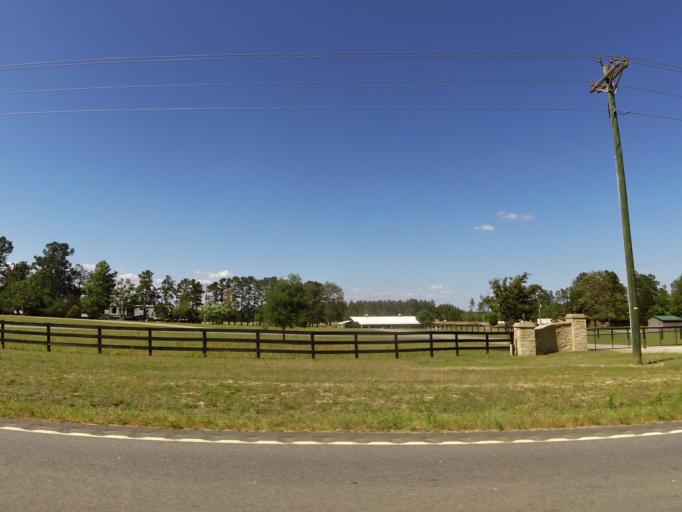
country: US
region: South Carolina
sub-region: Aiken County
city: New Ellenton
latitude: 33.5131
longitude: -81.5711
